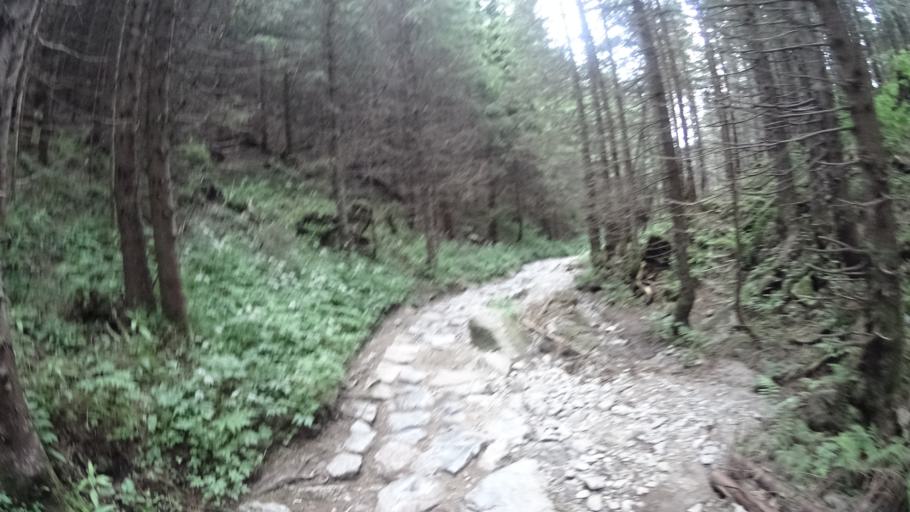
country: PL
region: Lesser Poland Voivodeship
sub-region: Powiat tatrzanski
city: Zakopane
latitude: 49.2517
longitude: 19.9613
